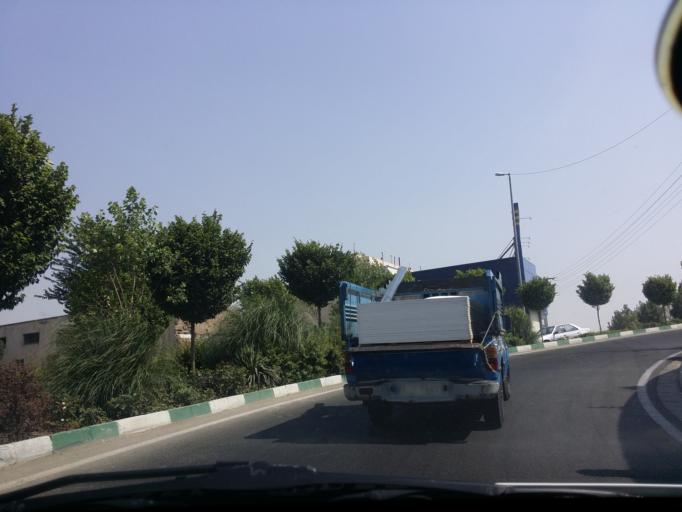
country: IR
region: Alborz
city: Karaj
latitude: 35.7903
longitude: 51.0045
